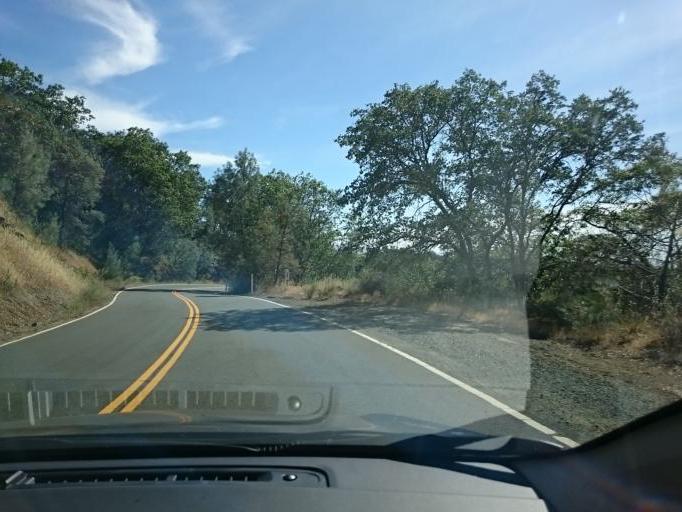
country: US
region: California
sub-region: Santa Clara County
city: East Foothills
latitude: 37.3375
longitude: -121.6662
